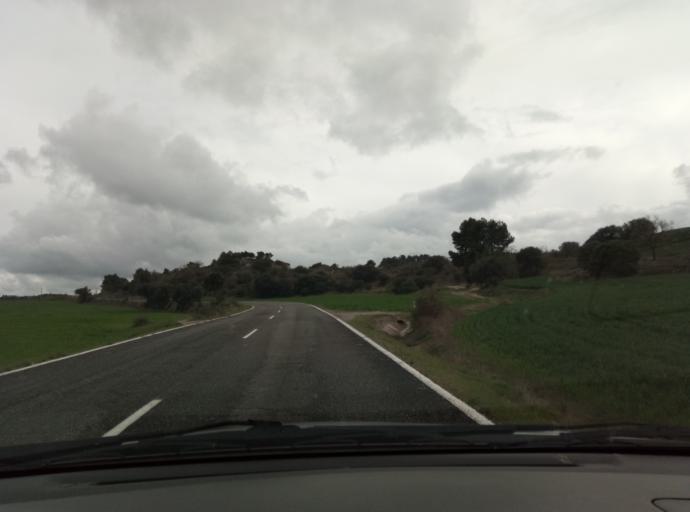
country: ES
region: Catalonia
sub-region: Provincia de Lleida
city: Sant Guim de Freixenet
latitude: 41.6141
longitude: 1.3430
